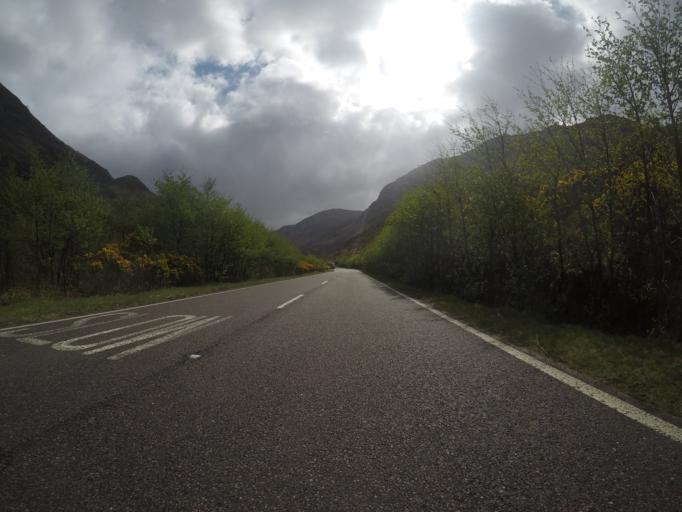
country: GB
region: Scotland
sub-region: Highland
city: Fort William
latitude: 57.1690
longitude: -5.3512
